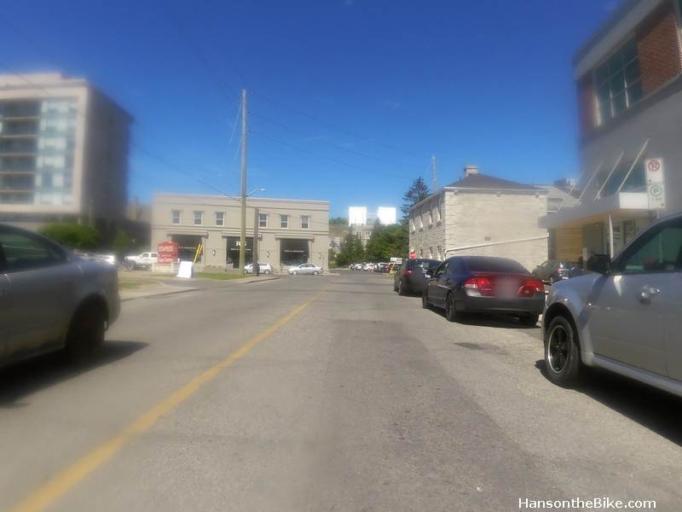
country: CA
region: Ontario
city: Kingston
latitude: 44.2335
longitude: -76.4831
